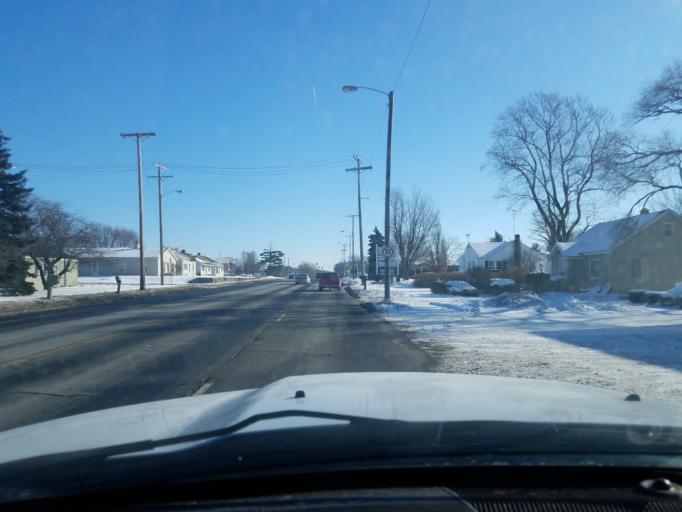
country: US
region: Indiana
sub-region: Noble County
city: Kendallville
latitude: 41.4522
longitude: -85.2630
